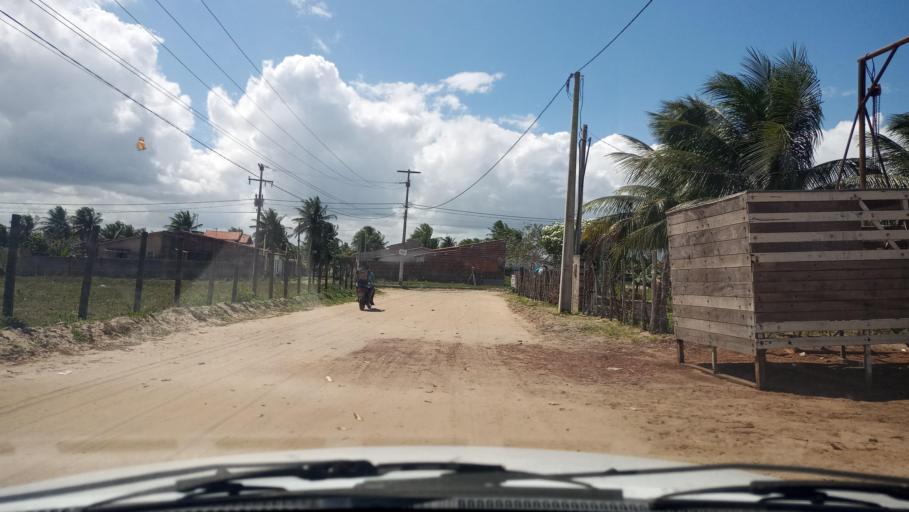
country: BR
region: Rio Grande do Norte
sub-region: Brejinho
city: Brejinho
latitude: -6.1934
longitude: -35.3640
